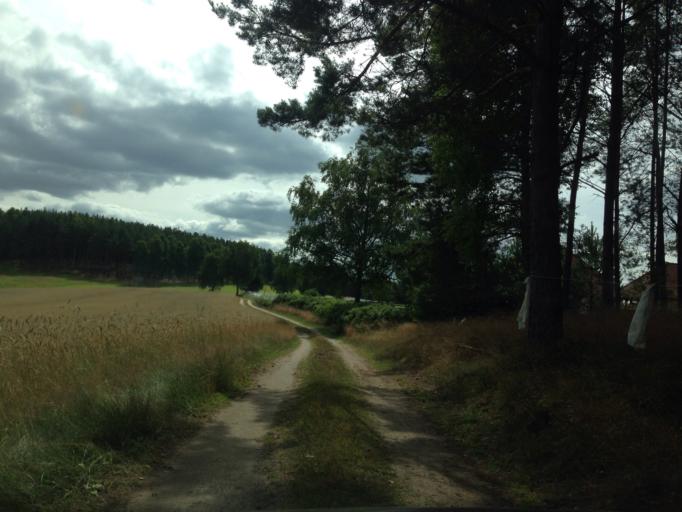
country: PL
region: Pomeranian Voivodeship
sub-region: Powiat bytowski
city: Studzienice
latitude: 54.0601
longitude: 17.6704
